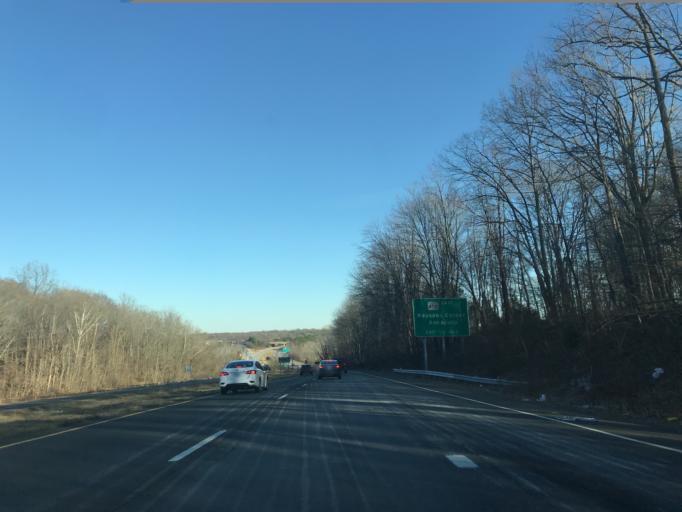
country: US
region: Maryland
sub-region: Prince George's County
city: Marlboro Meadows
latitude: 38.8116
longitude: -76.7168
